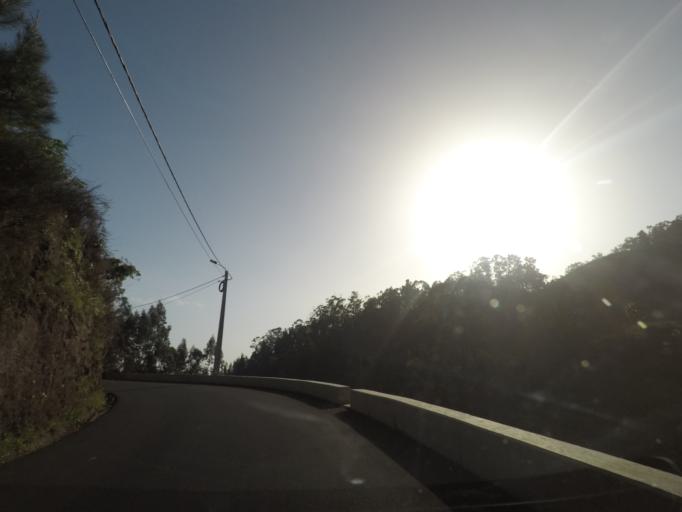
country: PT
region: Madeira
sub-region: Ribeira Brava
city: Campanario
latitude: 32.6746
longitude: -17.0044
